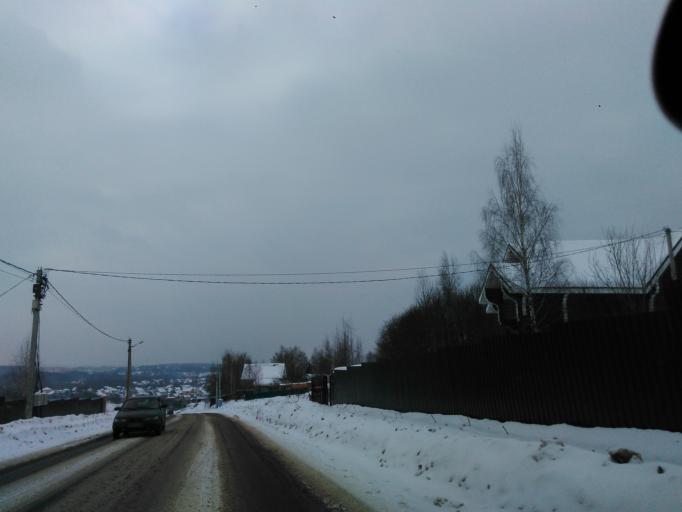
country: RU
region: Moskovskaya
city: Yakhroma
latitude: 56.2740
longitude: 37.4858
